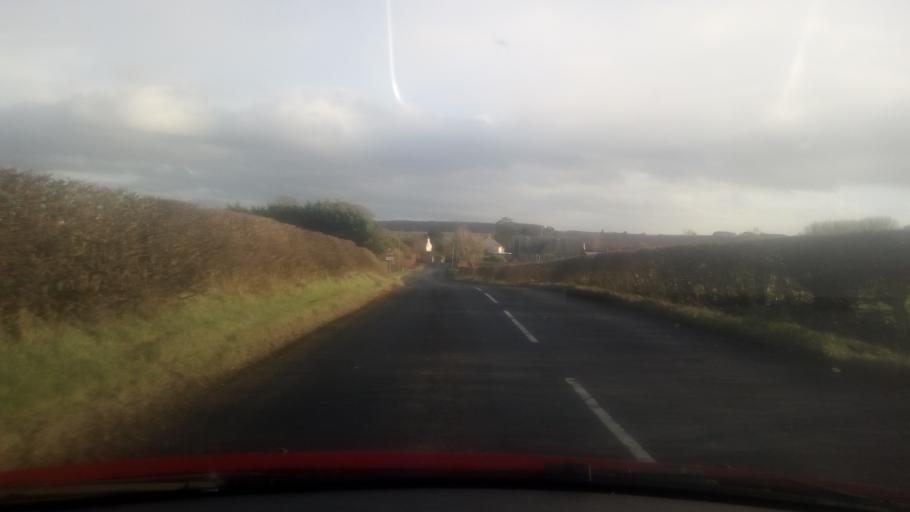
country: GB
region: Scotland
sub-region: The Scottish Borders
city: Kelso
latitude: 55.6305
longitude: -2.4184
